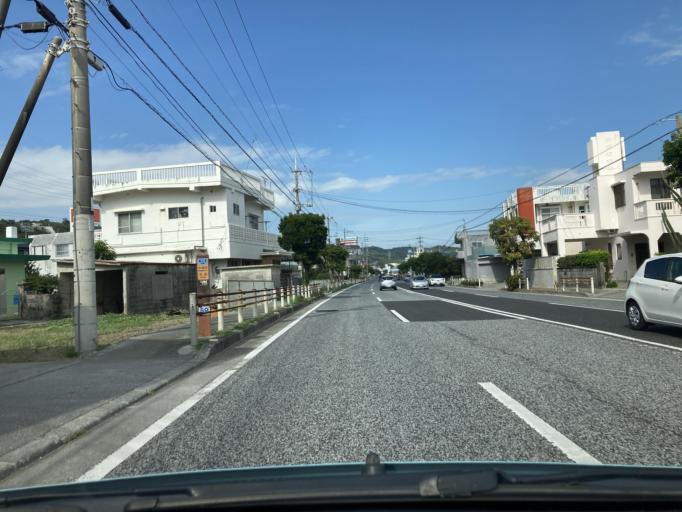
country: JP
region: Okinawa
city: Ginowan
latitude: 26.2602
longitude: 127.7871
